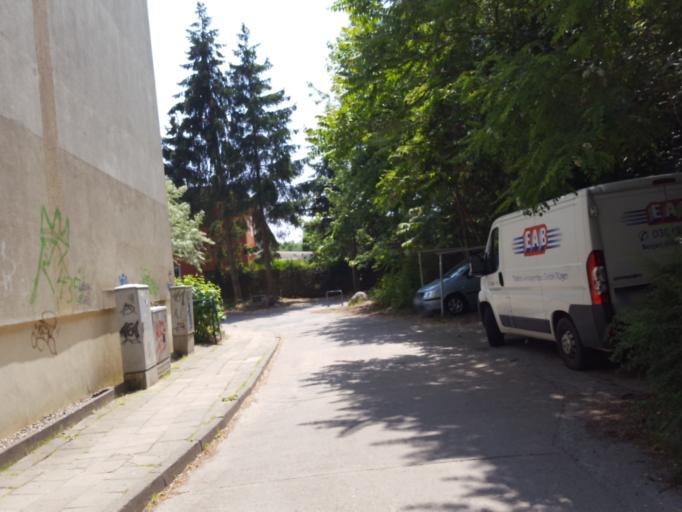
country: DE
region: Mecklenburg-Vorpommern
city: Kramerhof
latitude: 54.3235
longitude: 13.0490
